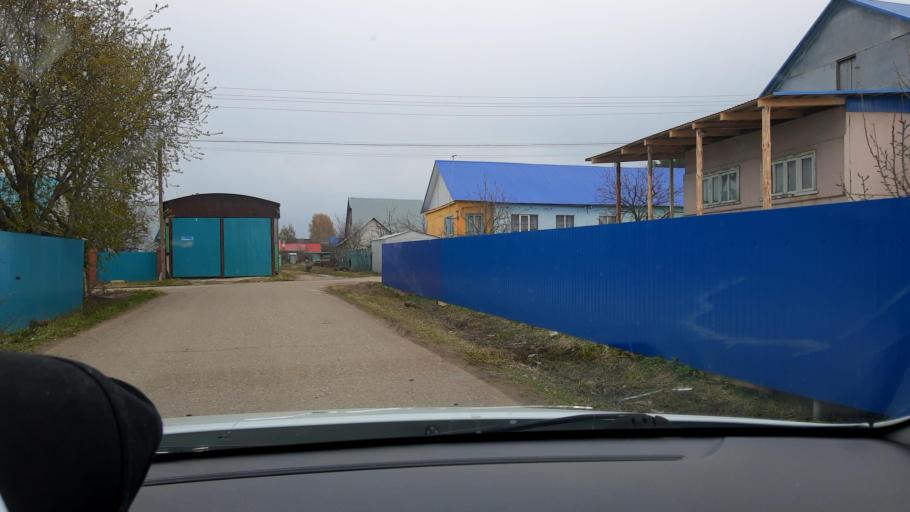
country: RU
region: Bashkortostan
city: Iglino
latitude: 54.7708
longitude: 56.5290
